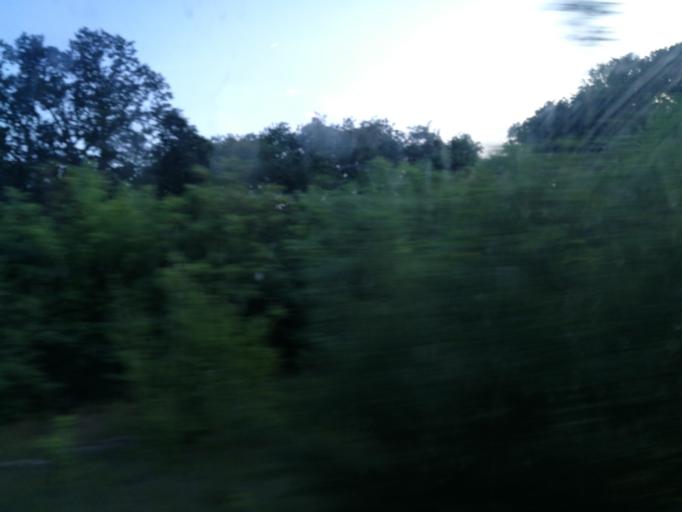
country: RO
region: Ilfov
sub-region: Comuna Buftea
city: Buciumeni
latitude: 44.5262
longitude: 25.9433
